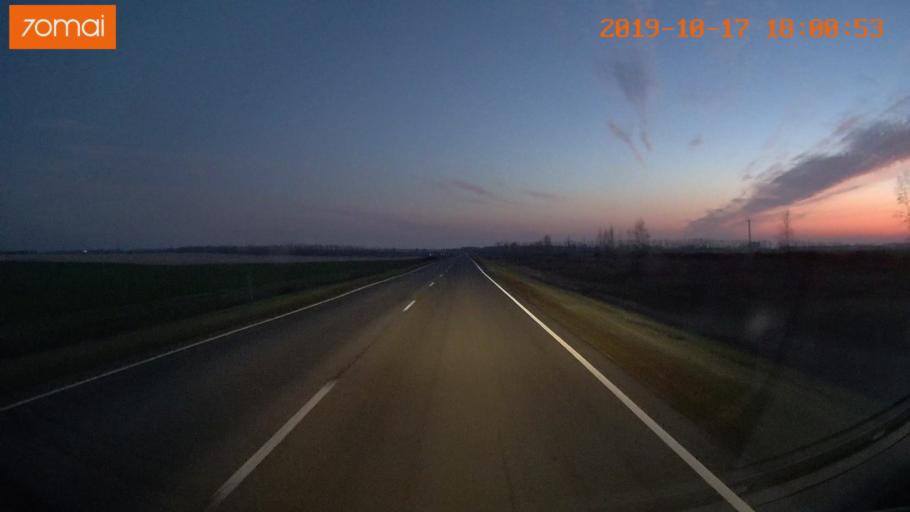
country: RU
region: Tula
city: Kurkino
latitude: 53.5151
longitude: 38.6128
